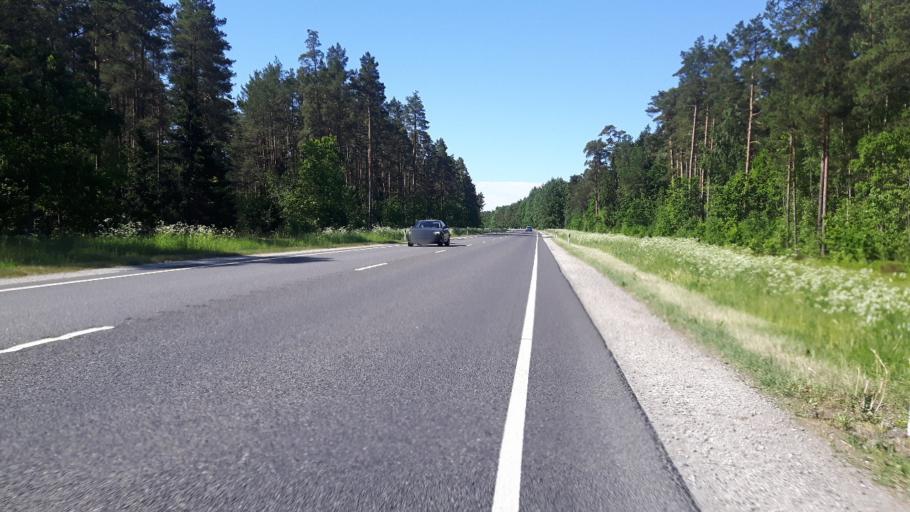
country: EE
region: Paernumaa
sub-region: Paikuse vald
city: Paikuse
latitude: 58.2759
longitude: 24.5629
